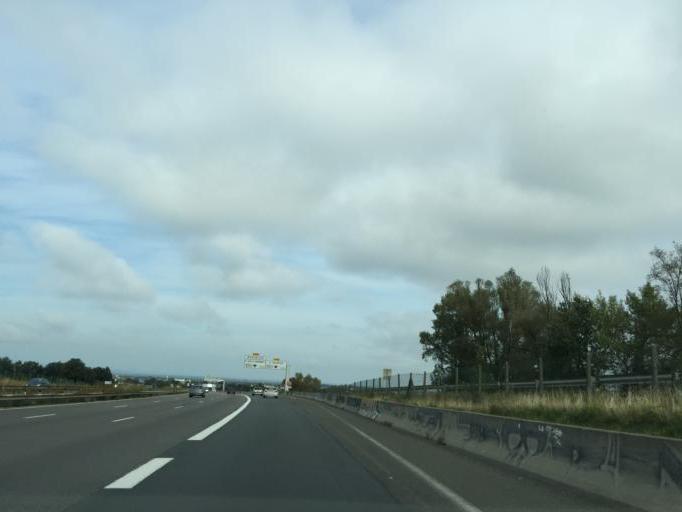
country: FR
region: Rhone-Alpes
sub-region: Departement de la Loire
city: La Fouillouse
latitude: 45.5151
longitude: 4.3004
